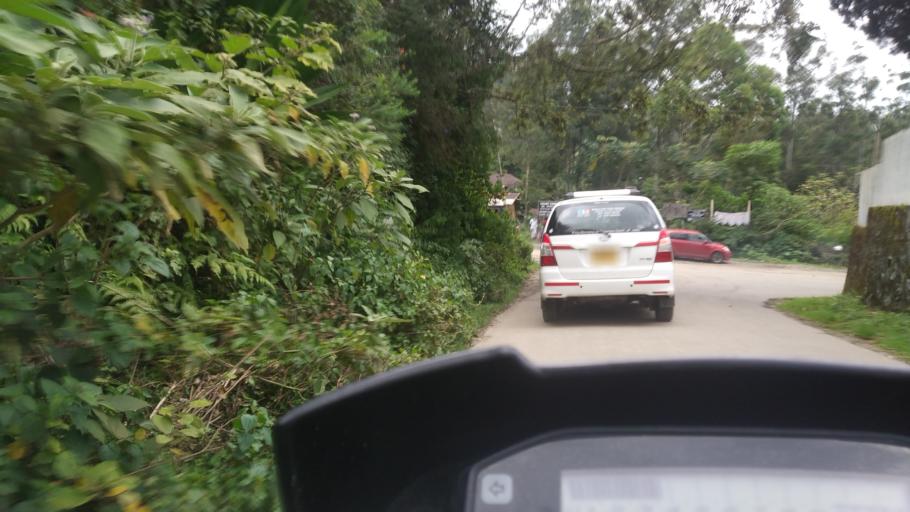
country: IN
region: Kerala
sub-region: Idukki
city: Munnar
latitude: 10.0674
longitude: 77.1074
